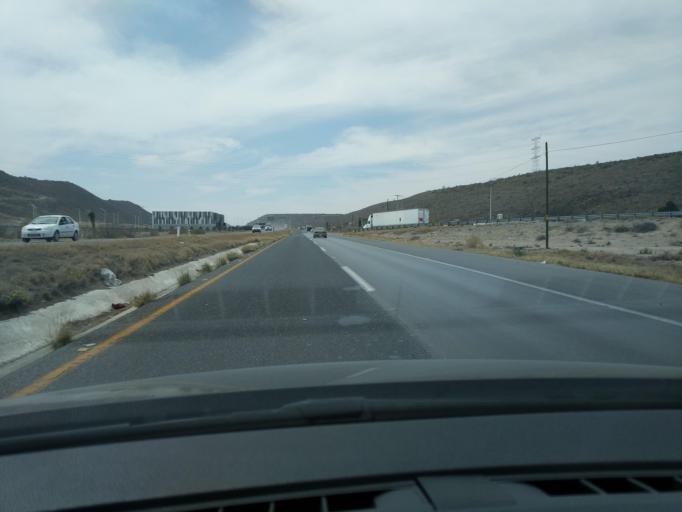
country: MX
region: Coahuila
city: Saltillo
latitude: 25.4536
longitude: -101.0675
